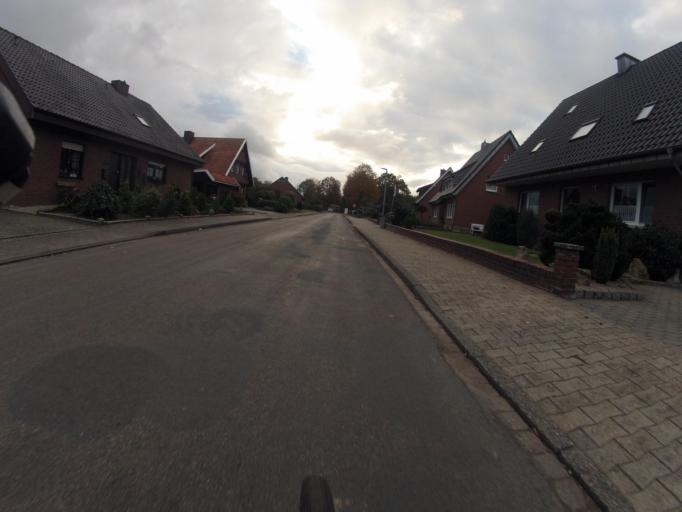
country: DE
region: North Rhine-Westphalia
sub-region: Regierungsbezirk Munster
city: Horstel
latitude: 52.2717
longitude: 7.5740
